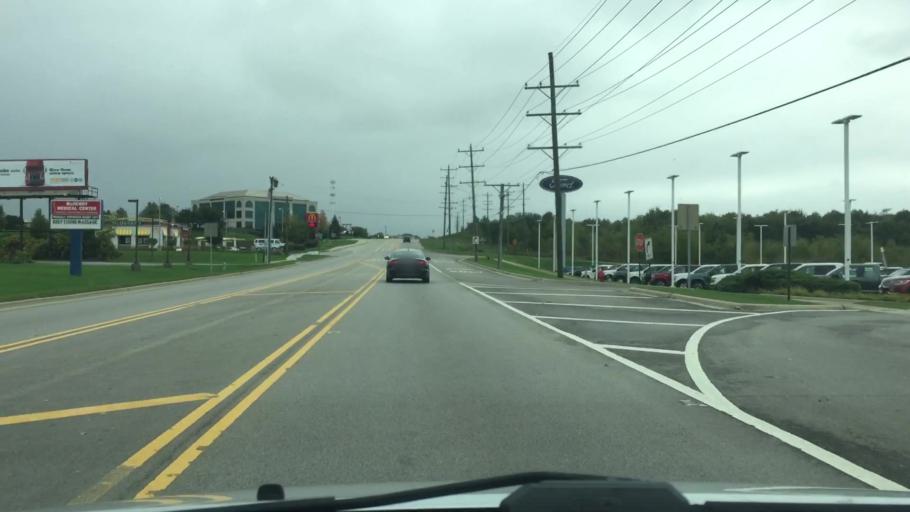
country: US
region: Illinois
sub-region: McHenry County
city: McHenry
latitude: 42.3275
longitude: -88.2744
